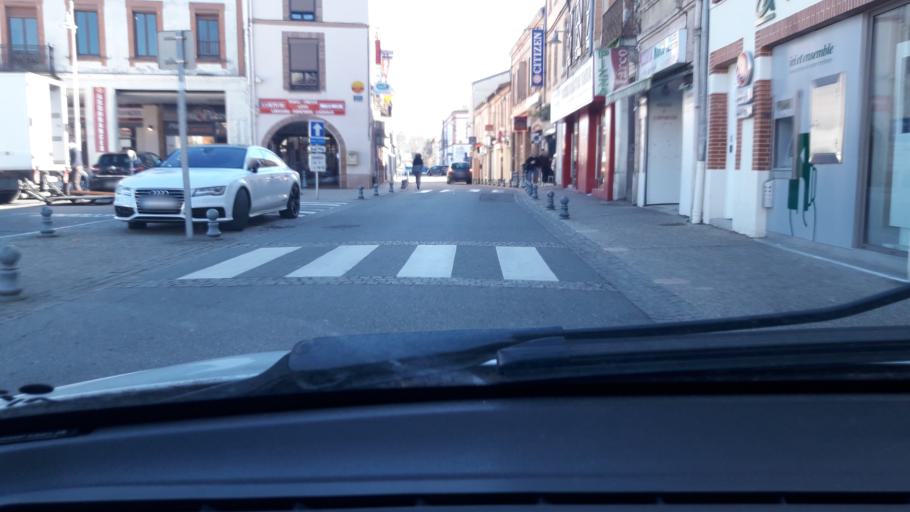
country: FR
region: Midi-Pyrenees
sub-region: Departement du Gers
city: Pujaudran
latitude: 43.6140
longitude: 1.0822
